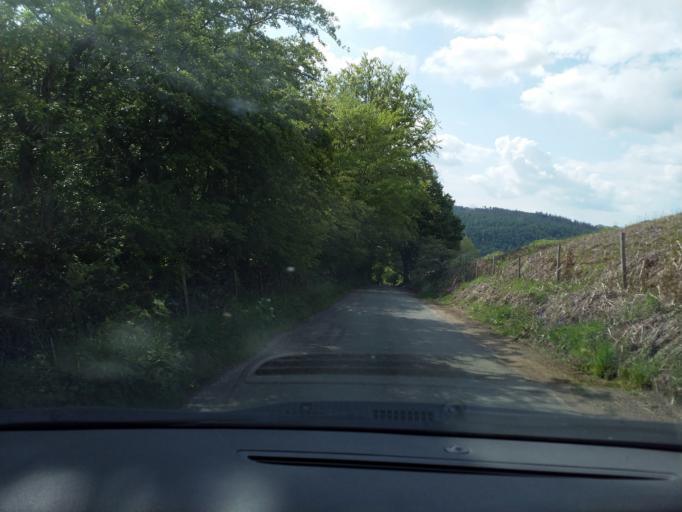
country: GB
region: England
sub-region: Derbyshire
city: Hathersage
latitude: 53.3562
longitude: -1.6909
